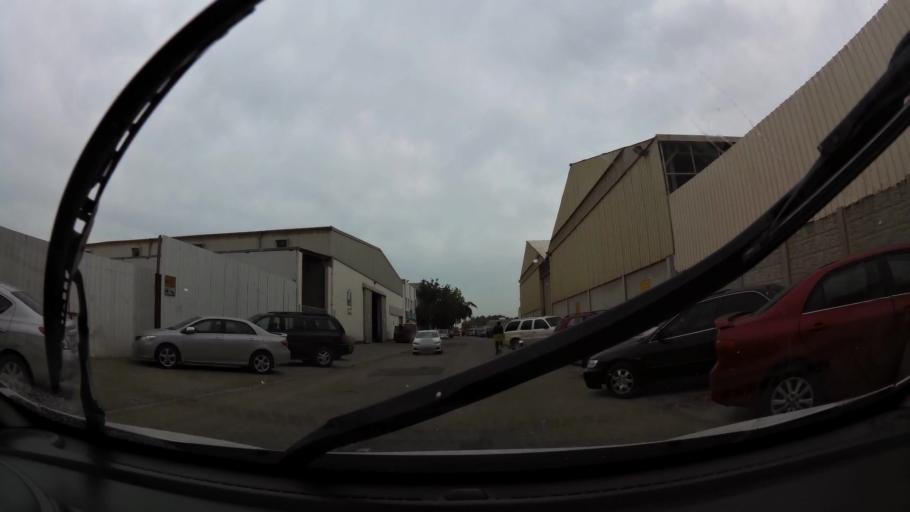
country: BH
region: Northern
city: Madinat `Isa
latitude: 26.1823
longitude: 50.5336
